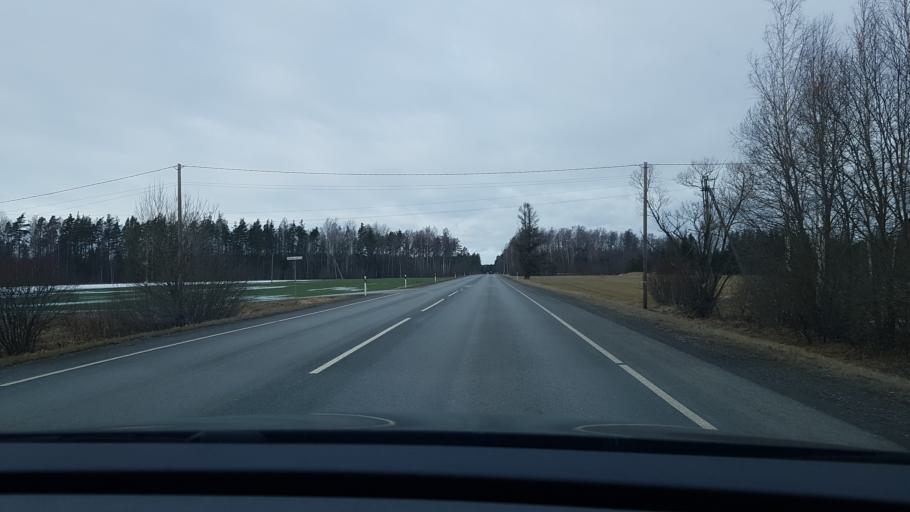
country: EE
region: Paernumaa
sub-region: Paikuse vald
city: Paikuse
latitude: 58.2374
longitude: 24.6941
